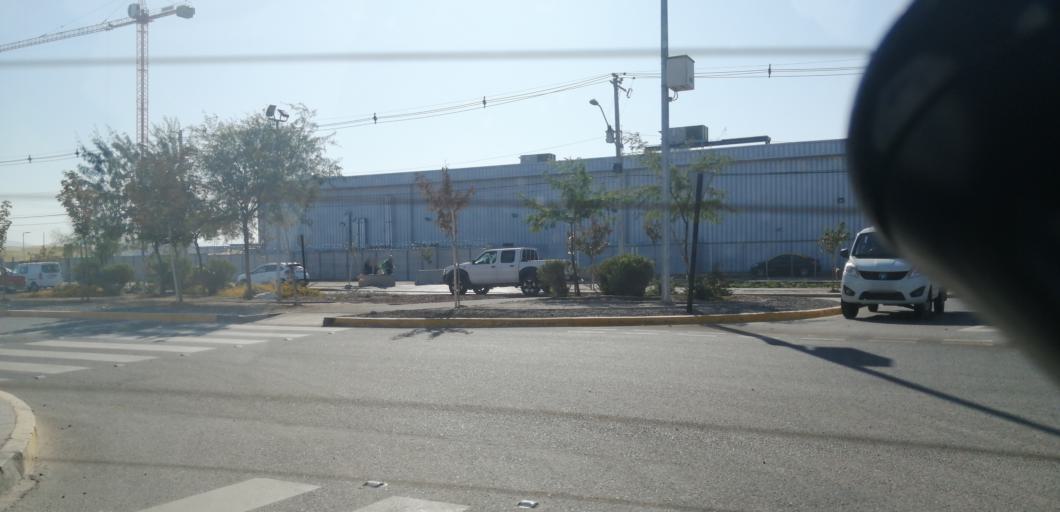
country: CL
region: Santiago Metropolitan
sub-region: Provincia de Santiago
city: Lo Prado
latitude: -33.4431
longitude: -70.7757
